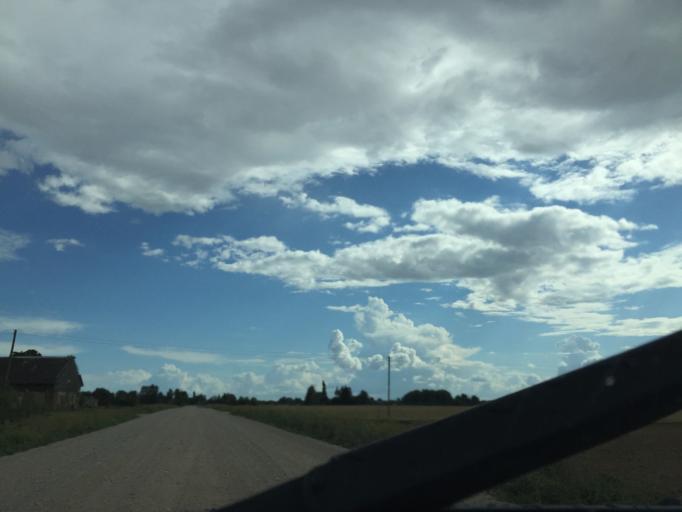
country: LT
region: Siauliu apskritis
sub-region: Joniskis
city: Joniskis
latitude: 56.3177
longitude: 23.5523
